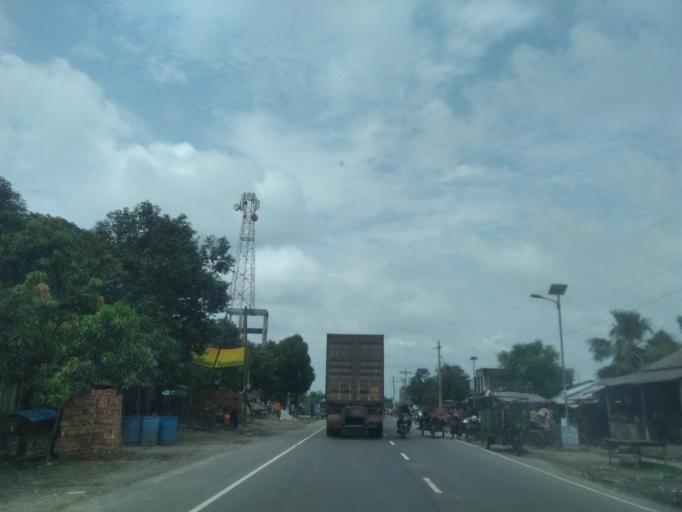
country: BD
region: Khulna
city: Kesabpur
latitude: 22.8122
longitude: 89.2452
